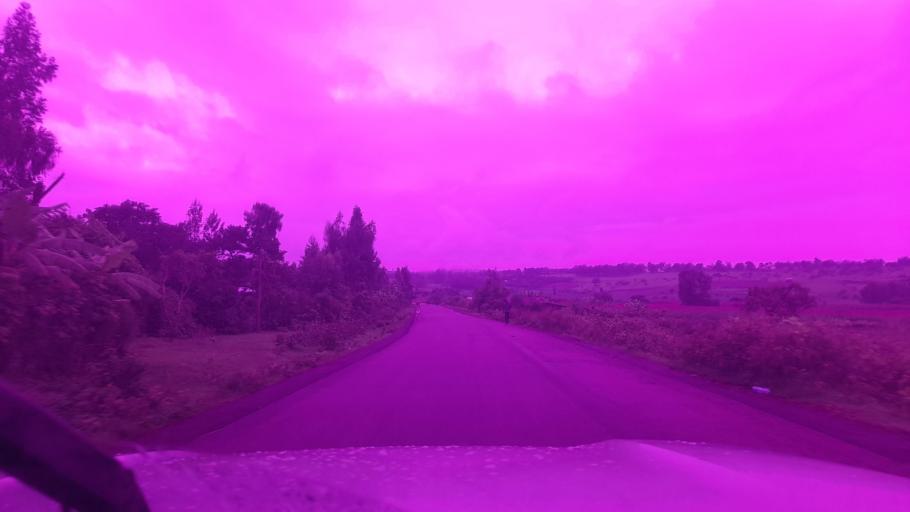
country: ET
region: Oromiya
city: Jima
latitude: 7.8299
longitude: 37.3473
